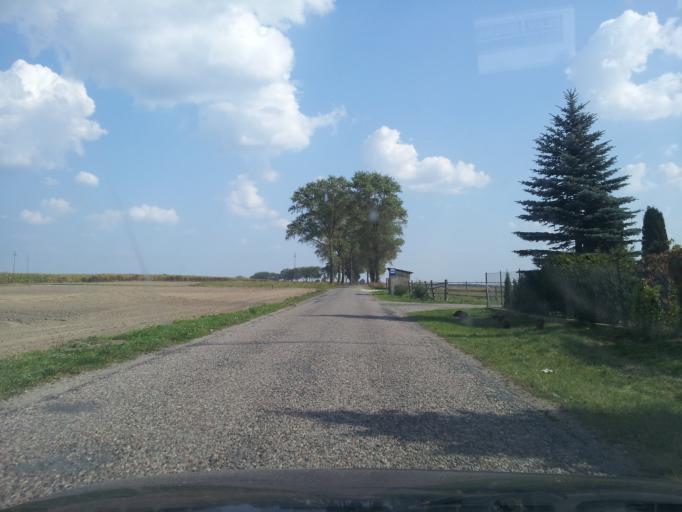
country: PL
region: Kujawsko-Pomorskie
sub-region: Powiat brodnicki
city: Gorzno
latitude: 53.1963
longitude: 19.6182
